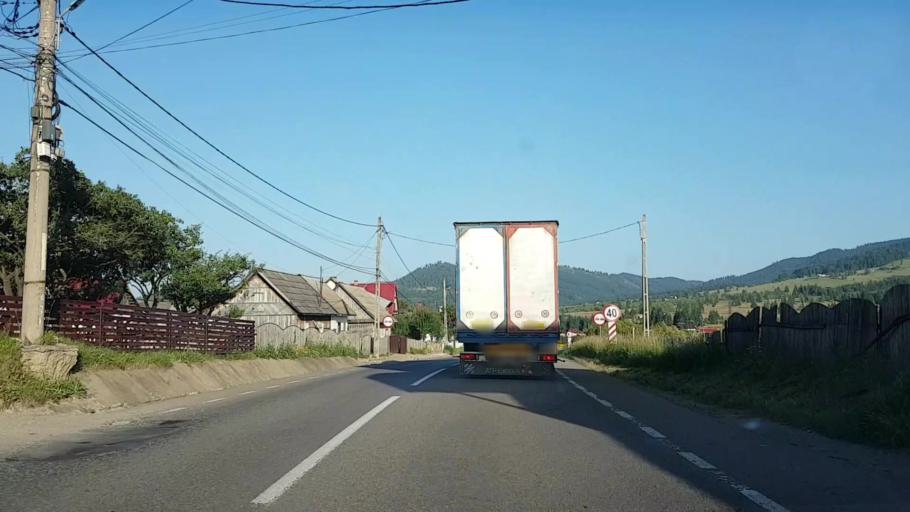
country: RO
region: Suceava
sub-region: Comuna Dorna Candrenilor
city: Dorna Candrenilor
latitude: 47.3584
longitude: 25.2333
